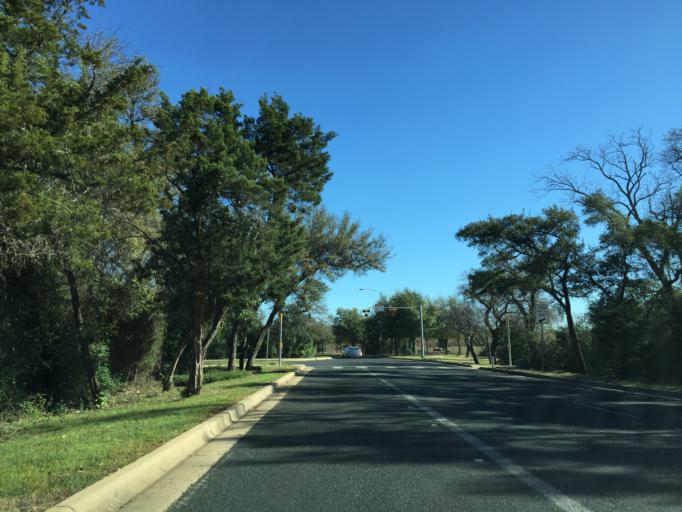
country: US
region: Texas
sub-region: Williamson County
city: Jollyville
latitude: 30.4291
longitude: -97.7414
